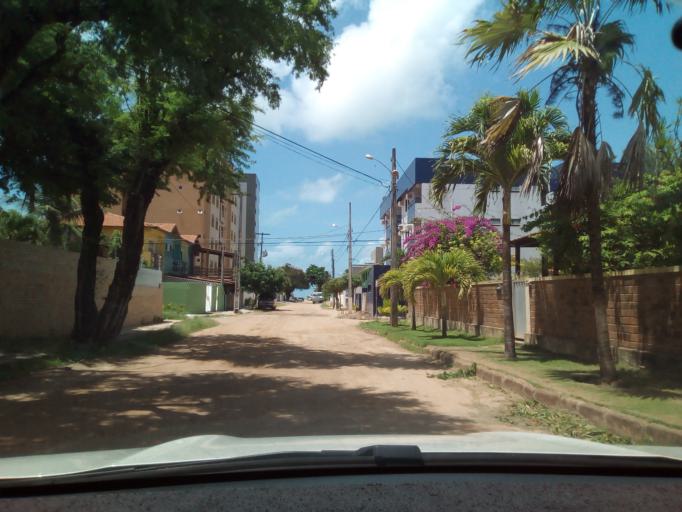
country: BR
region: Paraiba
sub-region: Cabedelo
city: Cabedelo
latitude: -7.0122
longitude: -34.8303
